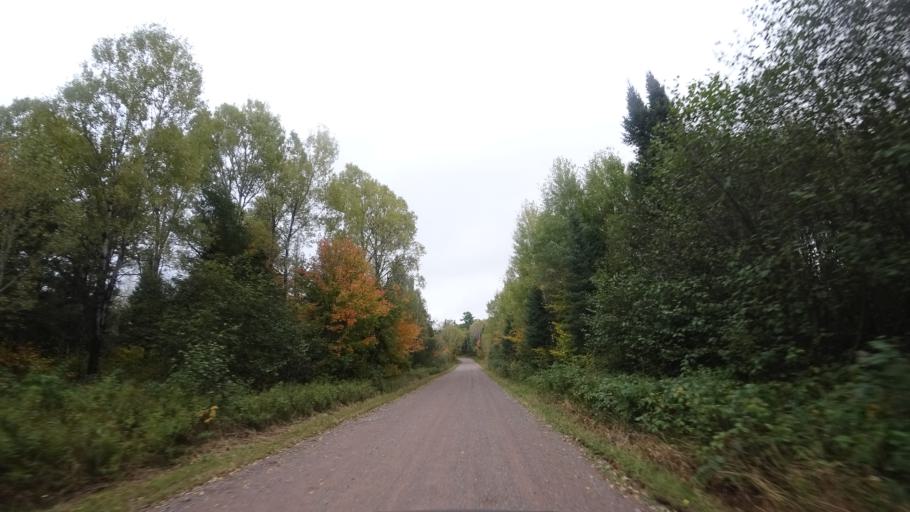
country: US
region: Wisconsin
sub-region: Sawyer County
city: Little Round Lake
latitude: 46.0742
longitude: -90.9927
